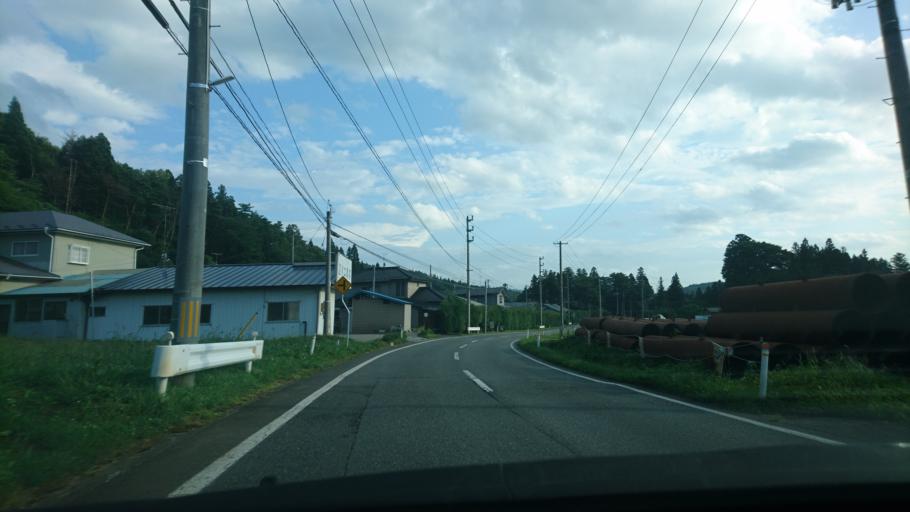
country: JP
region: Iwate
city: Mizusawa
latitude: 39.0287
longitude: 141.2946
